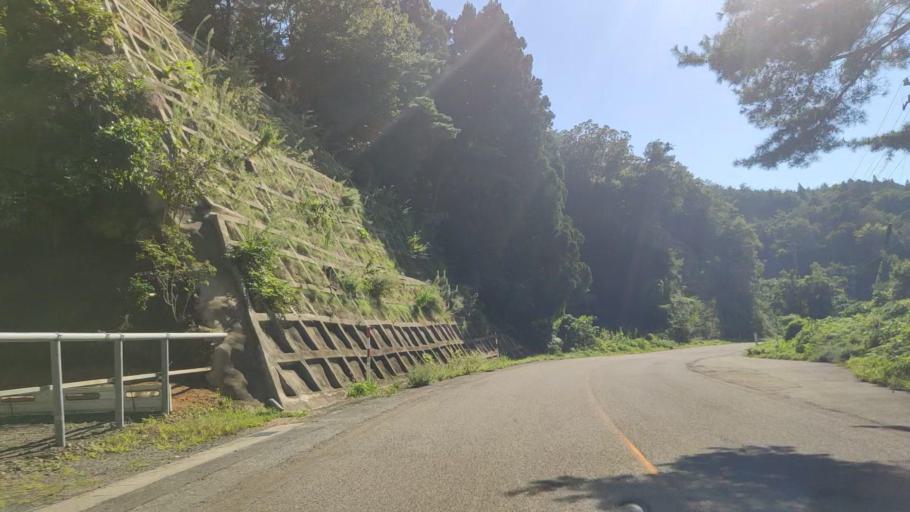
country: JP
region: Ishikawa
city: Nanao
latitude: 37.3162
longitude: 137.1647
